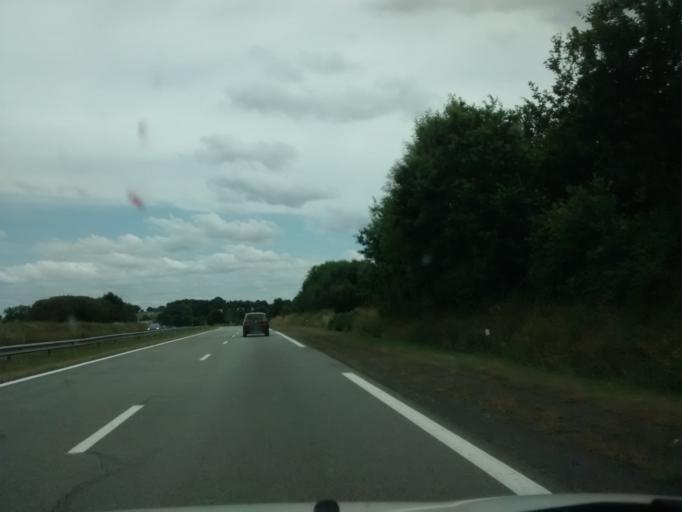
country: FR
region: Brittany
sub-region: Departement d'Ille-et-Vilaine
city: Quedillac
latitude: 48.2388
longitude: -2.1269
